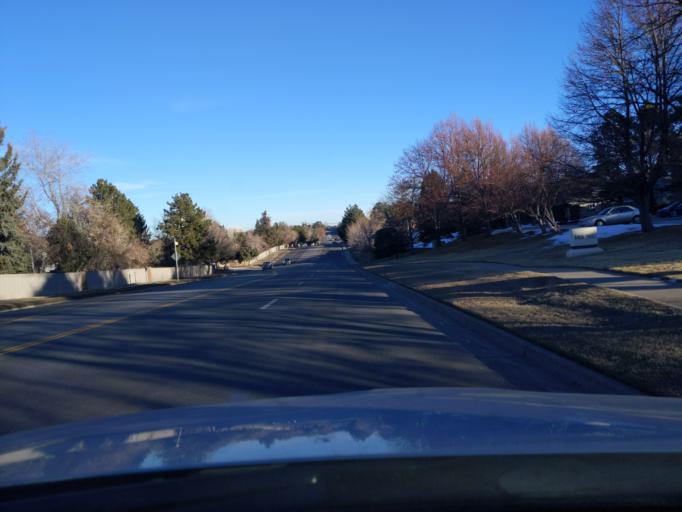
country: US
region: Colorado
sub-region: Arapahoe County
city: Centennial
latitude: 39.5726
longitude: -104.8856
